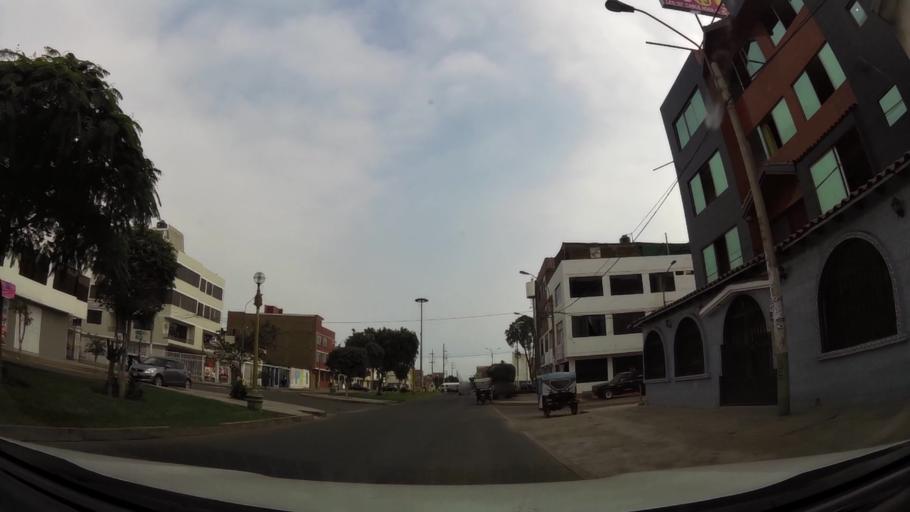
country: PE
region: Callao
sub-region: Callao
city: Callao
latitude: -12.0195
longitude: -77.0962
